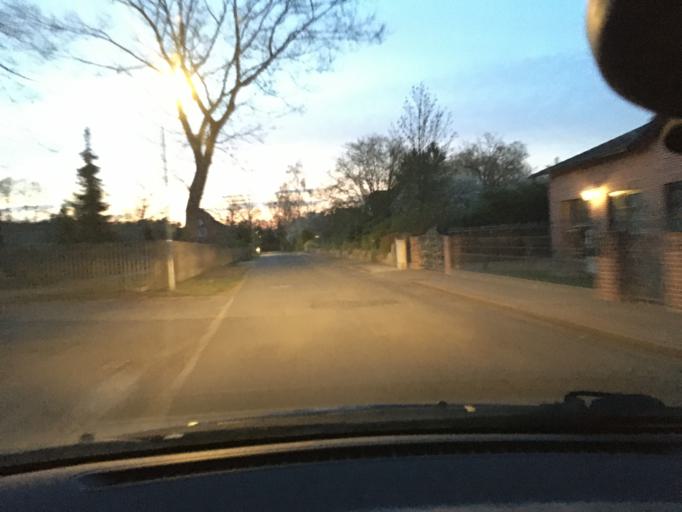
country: DE
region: Lower Saxony
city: Hanstedt
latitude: 53.2342
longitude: 10.0171
